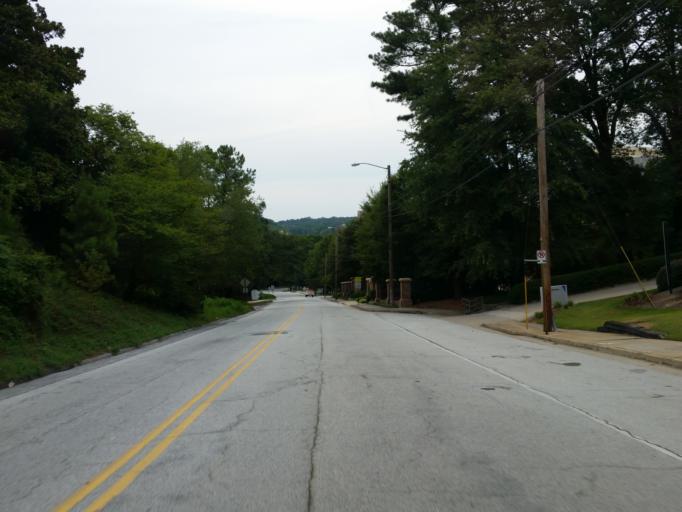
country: US
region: Georgia
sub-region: Cobb County
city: Vinings
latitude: 33.8423
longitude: -84.4278
